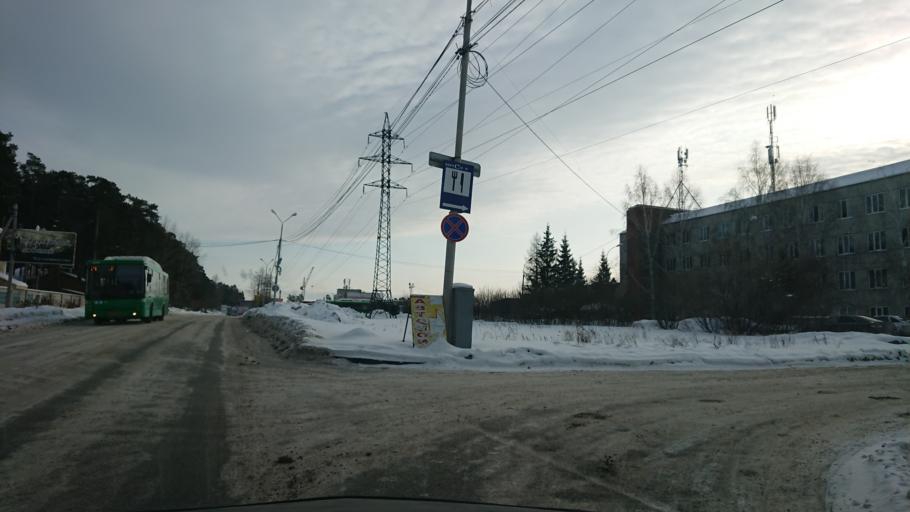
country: RU
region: Sverdlovsk
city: Sovkhoznyy
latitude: 56.7790
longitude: 60.5623
